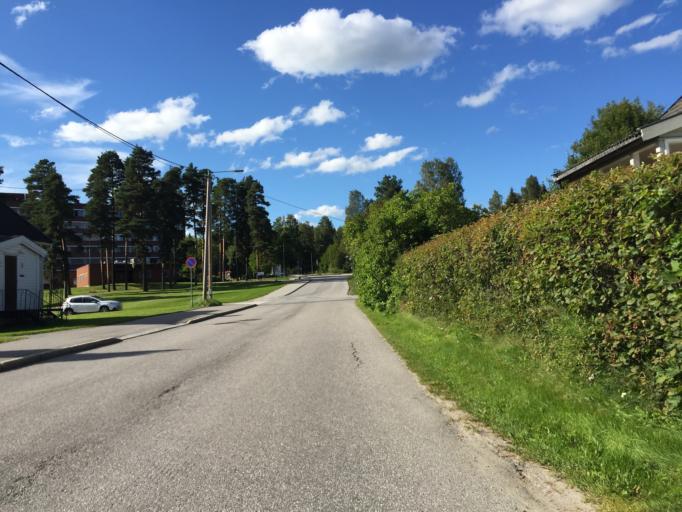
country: NO
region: Hedmark
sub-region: Kongsvinger
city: Kongsvinger
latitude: 60.1939
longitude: 11.9968
